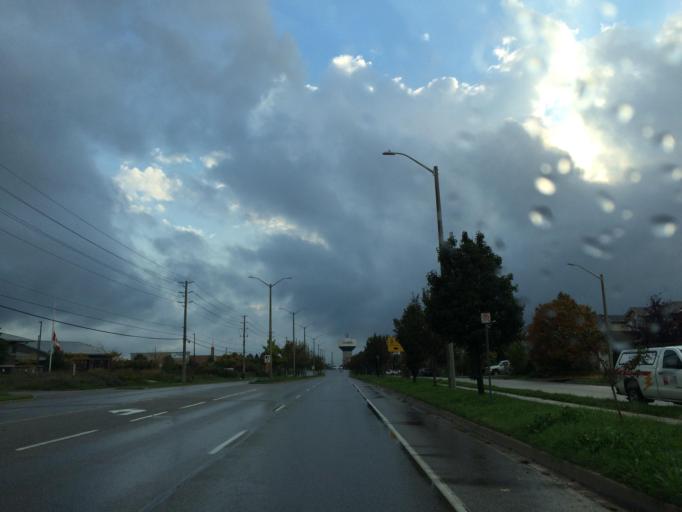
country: CA
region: Ontario
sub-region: Wellington County
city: Guelph
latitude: 43.4974
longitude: -80.1931
